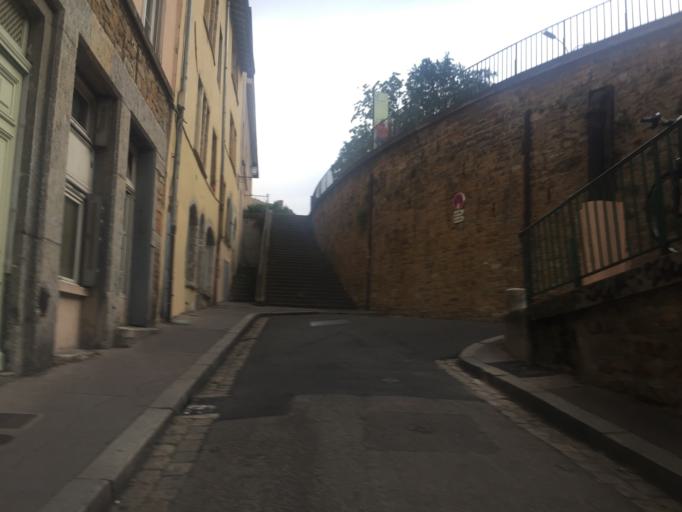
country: FR
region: Rhone-Alpes
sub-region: Departement du Rhone
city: Lyon
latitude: 45.7576
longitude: 4.8220
